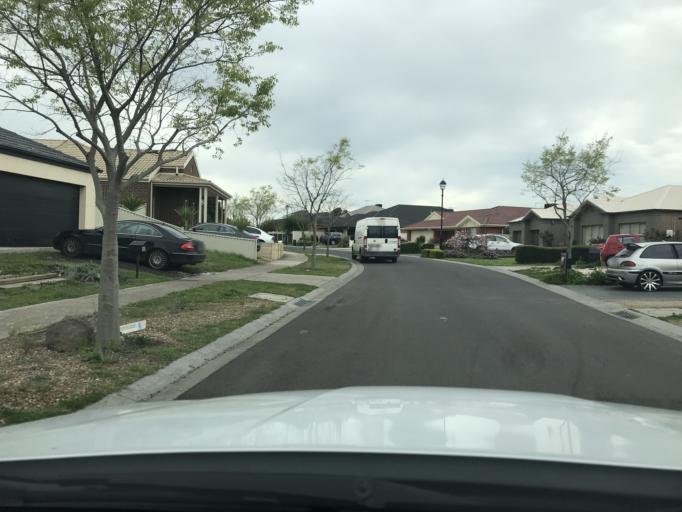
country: AU
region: Victoria
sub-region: Hume
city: Roxburgh Park
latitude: -37.6097
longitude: 144.9140
